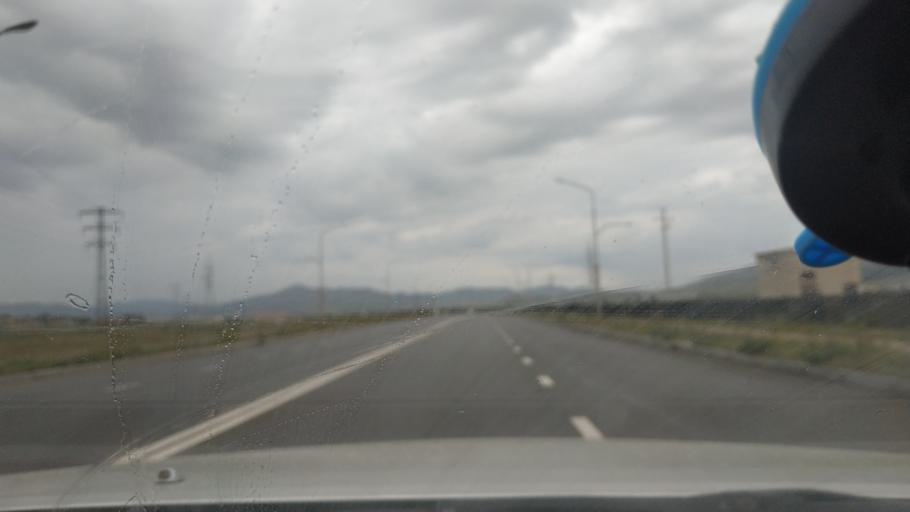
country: MN
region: Ulaanbaatar
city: Ulaanbaatar
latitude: 47.8992
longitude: 106.9974
